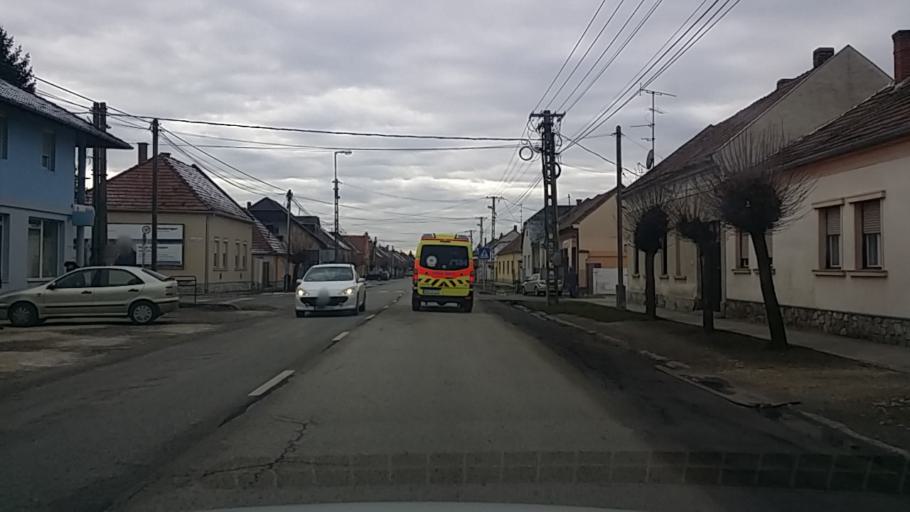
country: HU
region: Veszprem
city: Papa
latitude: 47.3212
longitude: 17.4692
